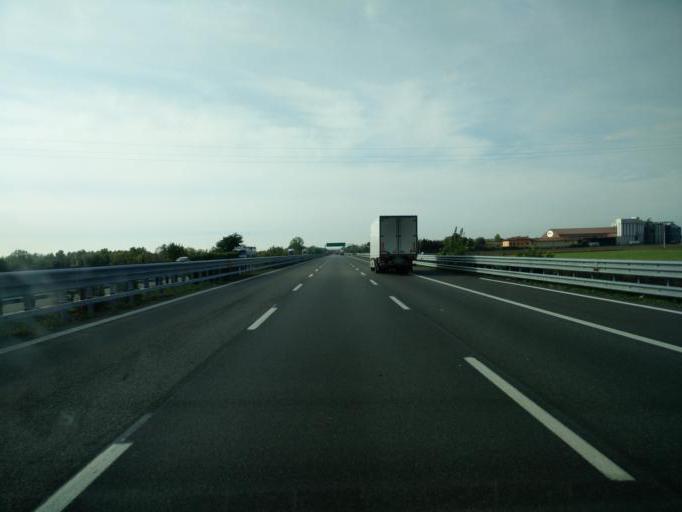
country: IT
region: Lombardy
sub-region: Provincia di Brescia
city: Leno
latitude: 45.3851
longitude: 10.1799
